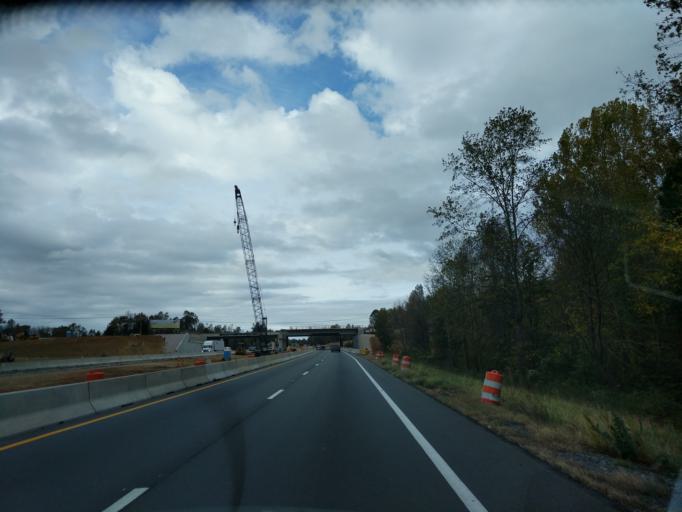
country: US
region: North Carolina
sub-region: Rowan County
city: China Grove
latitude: 35.5697
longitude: -80.5597
